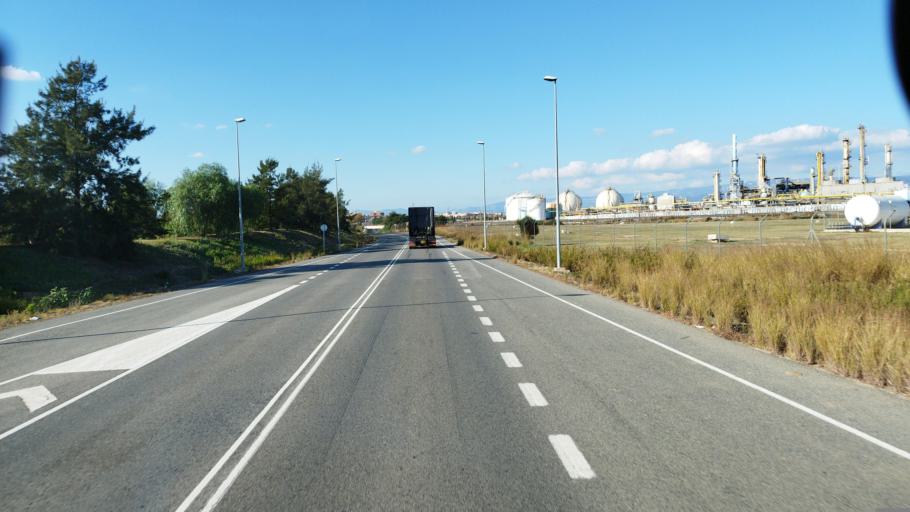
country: ES
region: Catalonia
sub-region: Provincia de Tarragona
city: Vila-seca
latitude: 41.1011
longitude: 1.1643
